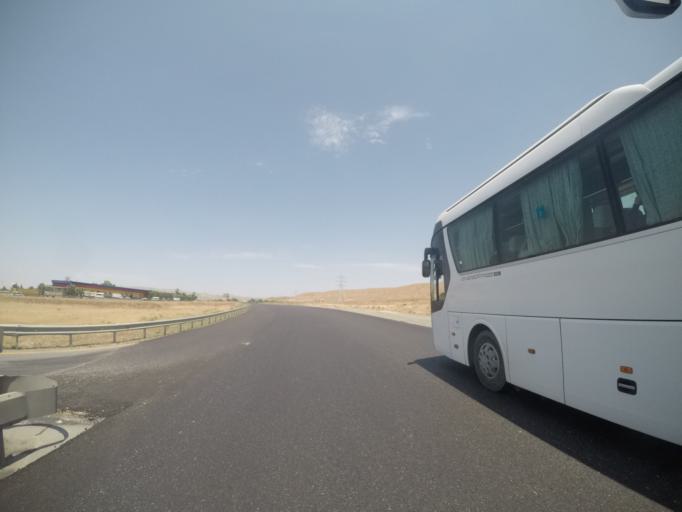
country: AZ
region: Haciqabul
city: Haciqabul
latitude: 40.0177
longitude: 48.9549
